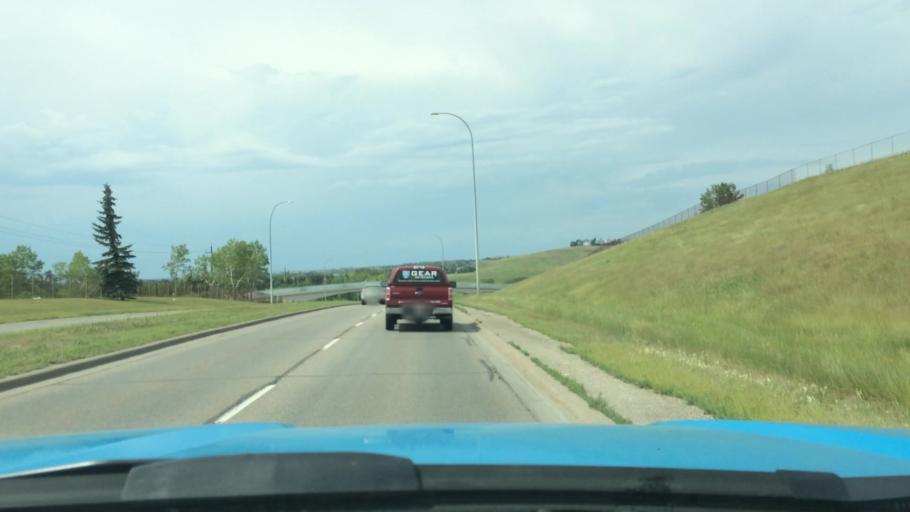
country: CA
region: Alberta
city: Calgary
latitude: 51.1004
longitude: -114.1221
